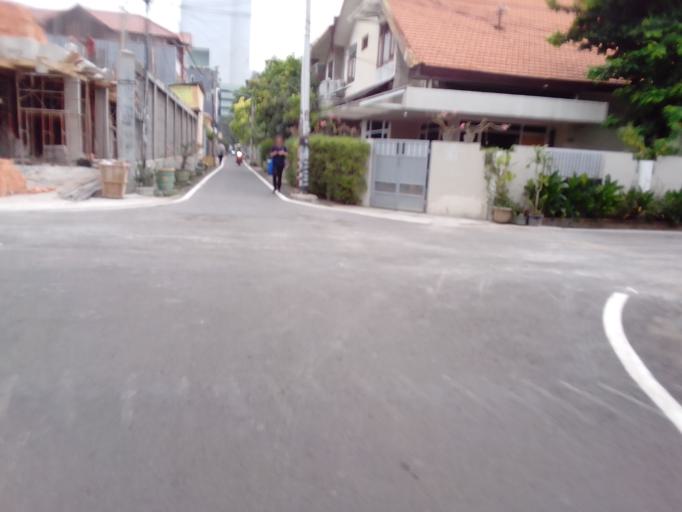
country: ID
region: Jakarta Raya
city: Jakarta
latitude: -6.1714
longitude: 106.8127
